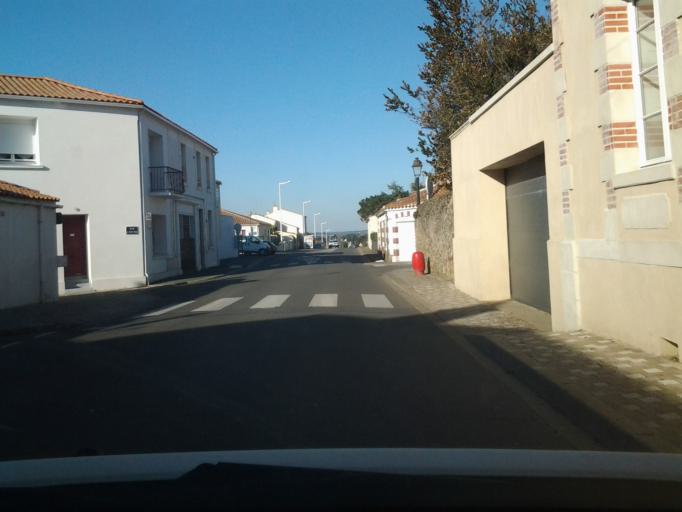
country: FR
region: Pays de la Loire
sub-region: Departement de la Vendee
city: Olonne-sur-Mer
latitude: 46.5372
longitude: -1.7723
